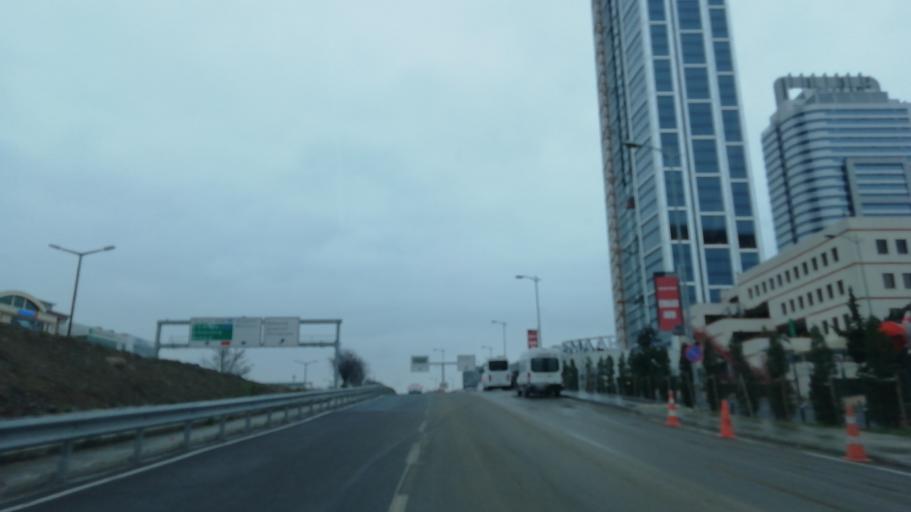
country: TR
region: Istanbul
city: UEskuedar
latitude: 41.0054
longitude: 29.0689
